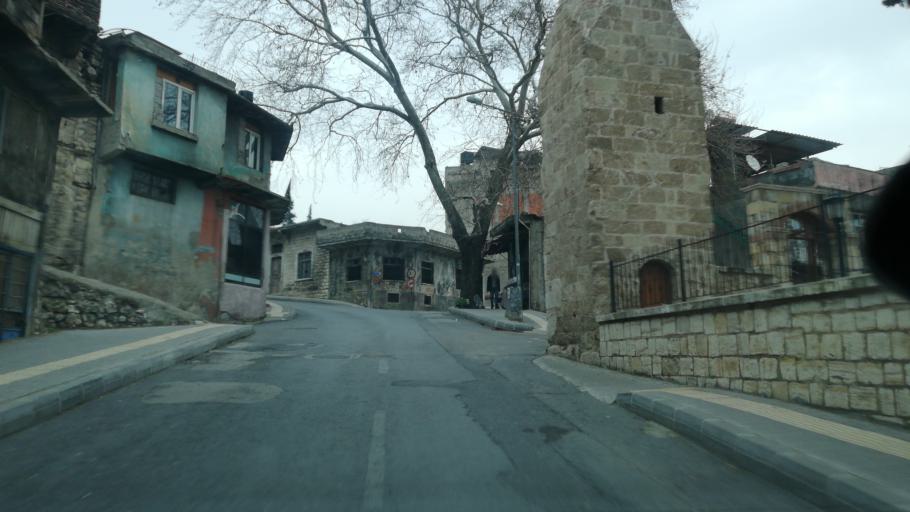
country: TR
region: Kahramanmaras
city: Kahramanmaras
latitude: 37.5873
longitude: 36.9307
